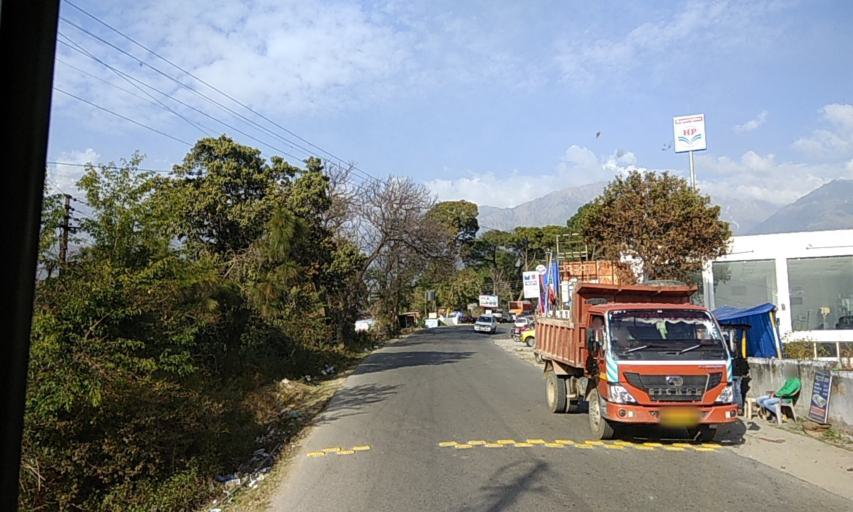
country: IN
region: Himachal Pradesh
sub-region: Kangra
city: Palampur
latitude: 32.0959
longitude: 76.5305
